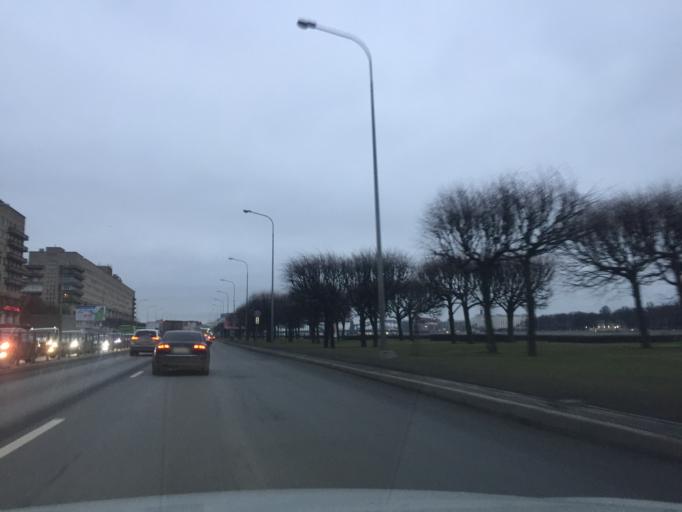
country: RU
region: Leningrad
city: Finlyandskiy
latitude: 59.9529
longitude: 30.4075
